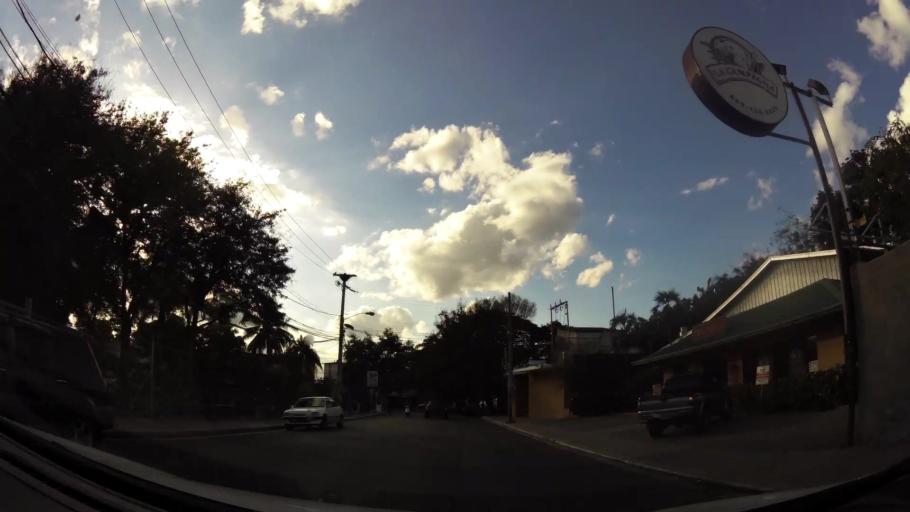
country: DO
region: Santiago
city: Santiago de los Caballeros
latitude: 19.4602
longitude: -70.7017
